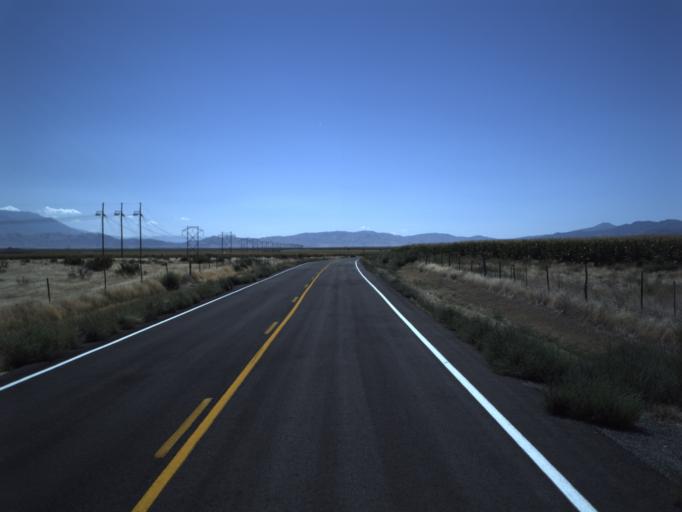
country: US
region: Utah
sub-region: Utah County
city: Genola
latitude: 40.1372
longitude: -111.9496
